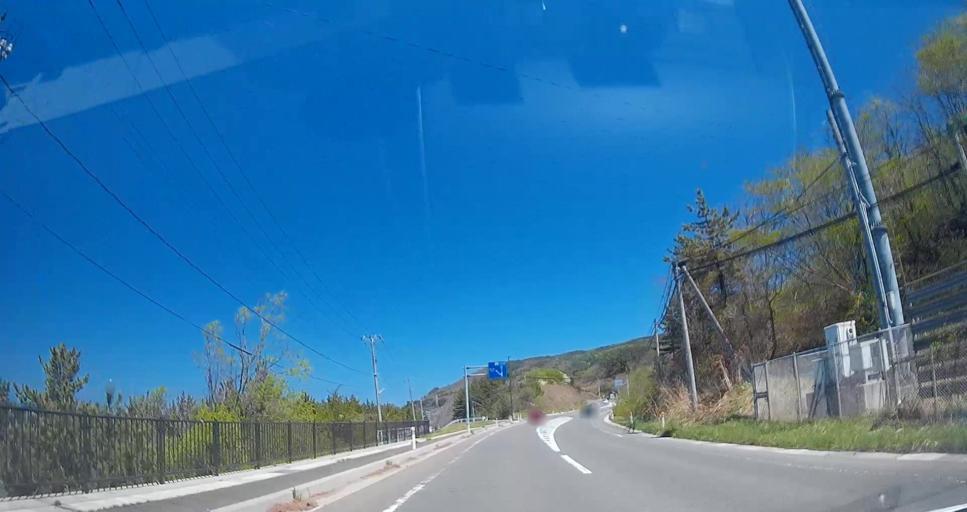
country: JP
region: Aomori
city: Mutsu
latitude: 41.3800
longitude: 141.3991
